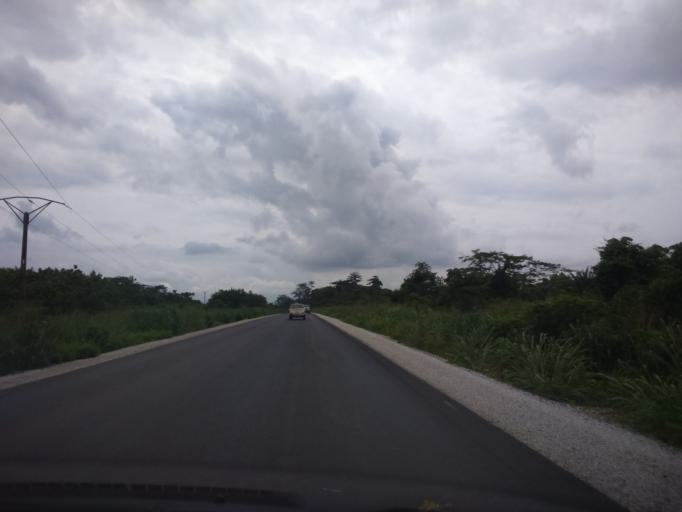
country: CI
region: Lagunes
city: Akoupe
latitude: 6.3140
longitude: -3.8311
